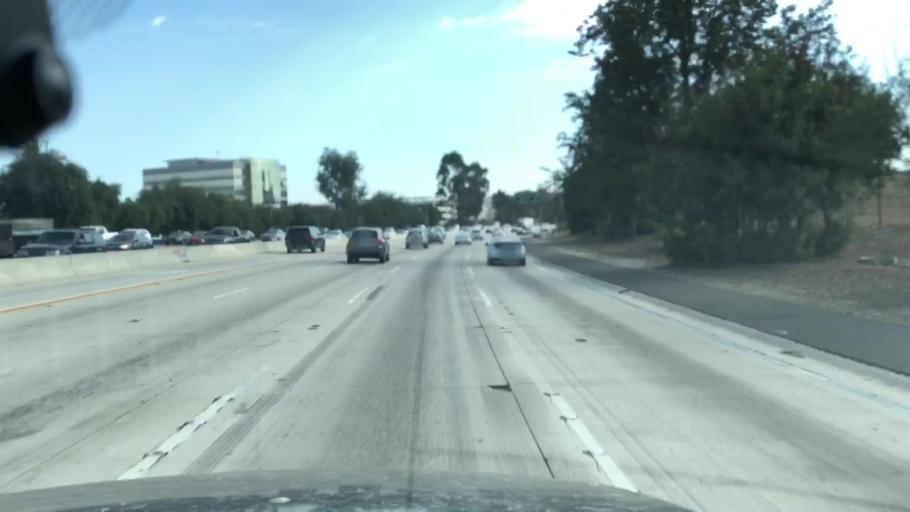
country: US
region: California
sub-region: Los Angeles County
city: Van Nuys
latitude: 34.1784
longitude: -118.4692
